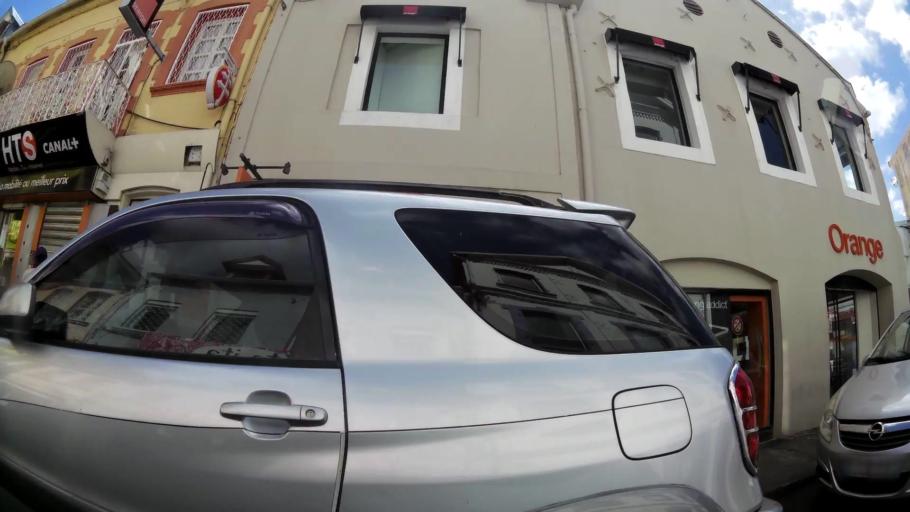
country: MQ
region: Martinique
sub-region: Martinique
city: Fort-de-France
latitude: 14.6042
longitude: -61.0709
